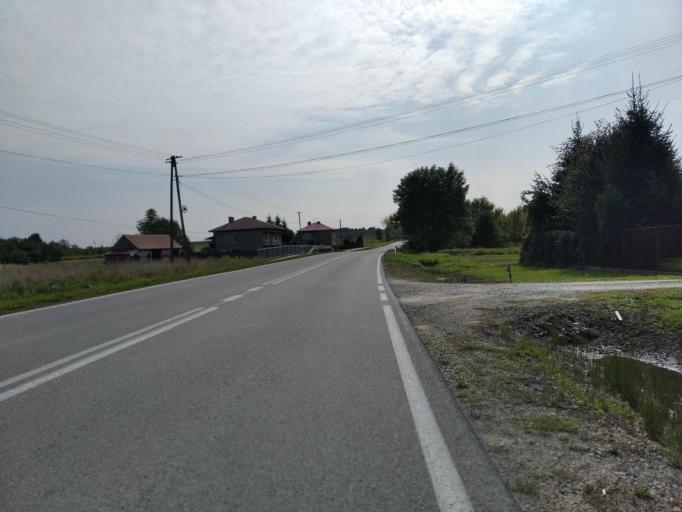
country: PL
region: Subcarpathian Voivodeship
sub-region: Powiat ropczycko-sedziszowski
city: Ostrow
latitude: 50.1119
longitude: 21.5911
